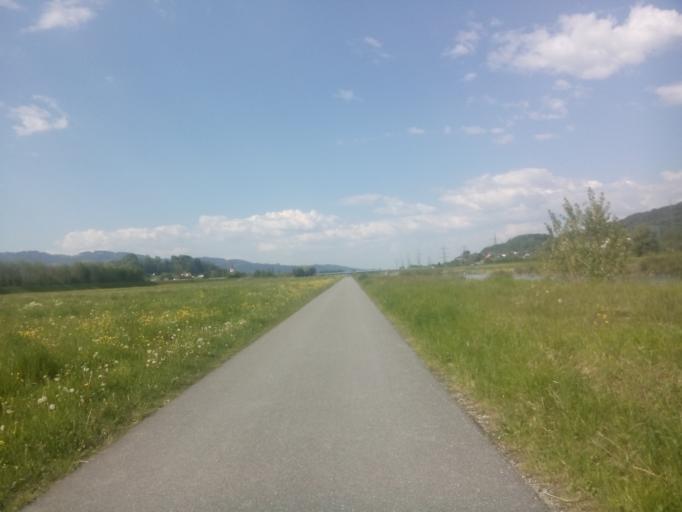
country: AT
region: Vorarlberg
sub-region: Politischer Bezirk Feldkirch
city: Koblach
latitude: 47.3230
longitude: 9.5900
